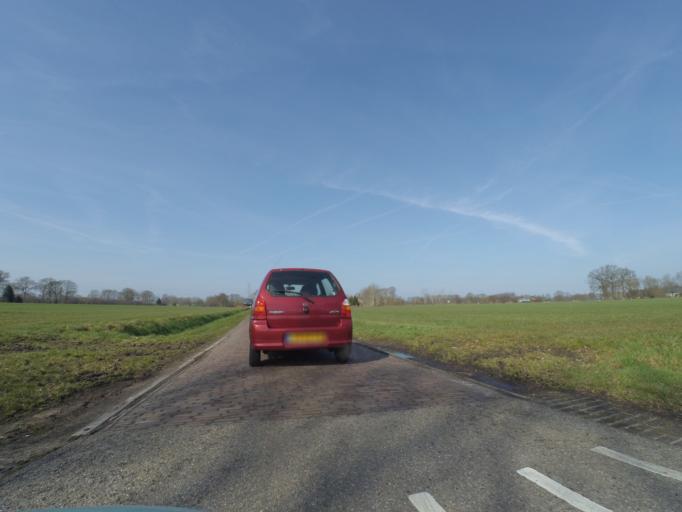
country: NL
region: Gelderland
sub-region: Gemeente Putten
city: Putten
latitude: 52.2287
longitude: 5.5981
